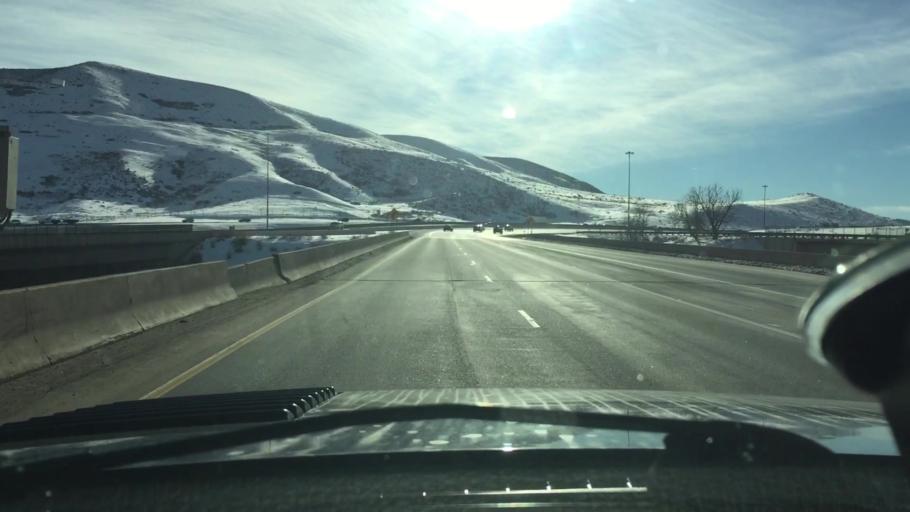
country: US
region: Colorado
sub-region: Jefferson County
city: West Pleasant View
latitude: 39.7124
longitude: -105.1949
